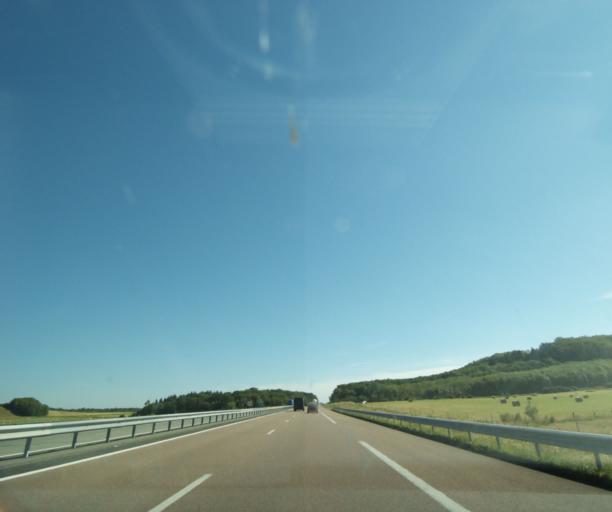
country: FR
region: Champagne-Ardenne
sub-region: Departement de la Haute-Marne
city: Saulxures
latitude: 48.0573
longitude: 5.5822
